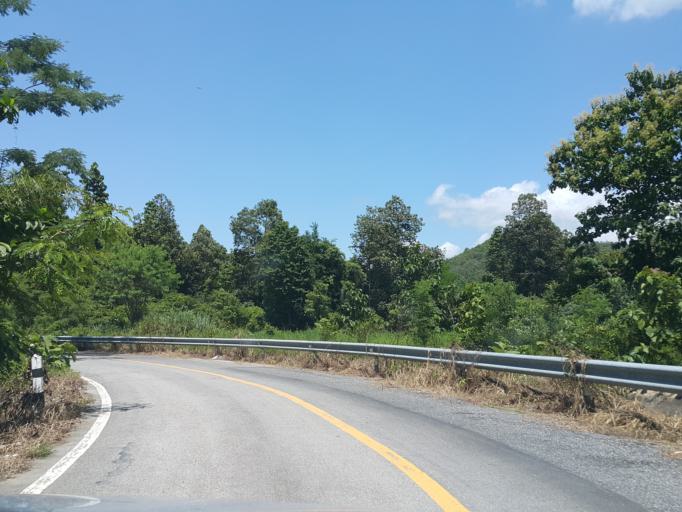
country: TH
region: Lamphun
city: Ban Thi
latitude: 18.6864
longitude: 99.1794
